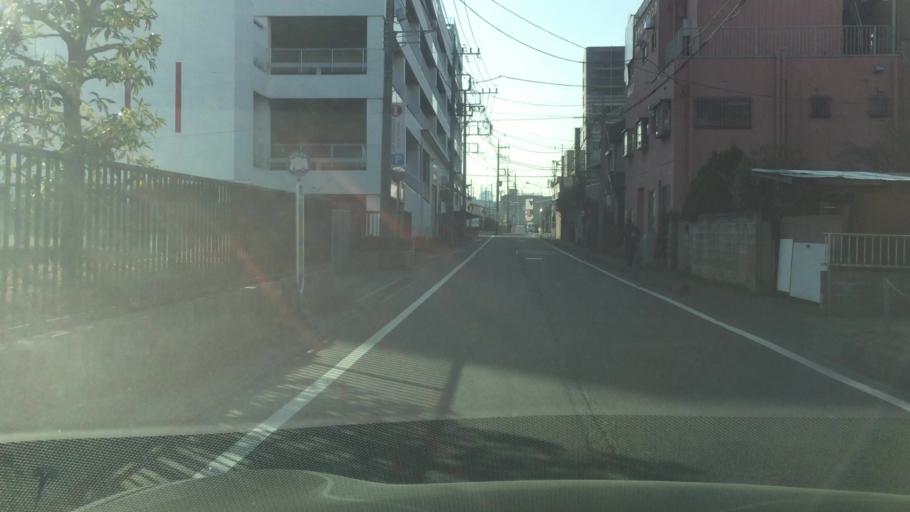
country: JP
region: Saitama
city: Ageoshimo
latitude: 35.9278
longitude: 139.6146
